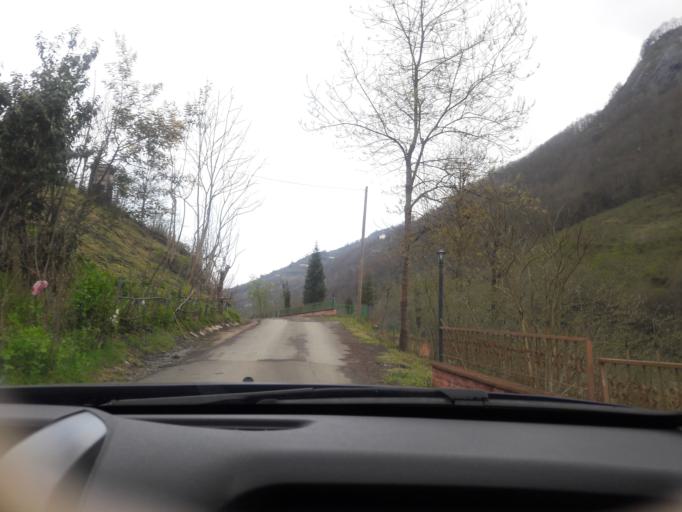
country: TR
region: Trabzon
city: Salpazari
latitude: 40.9694
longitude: 39.1972
